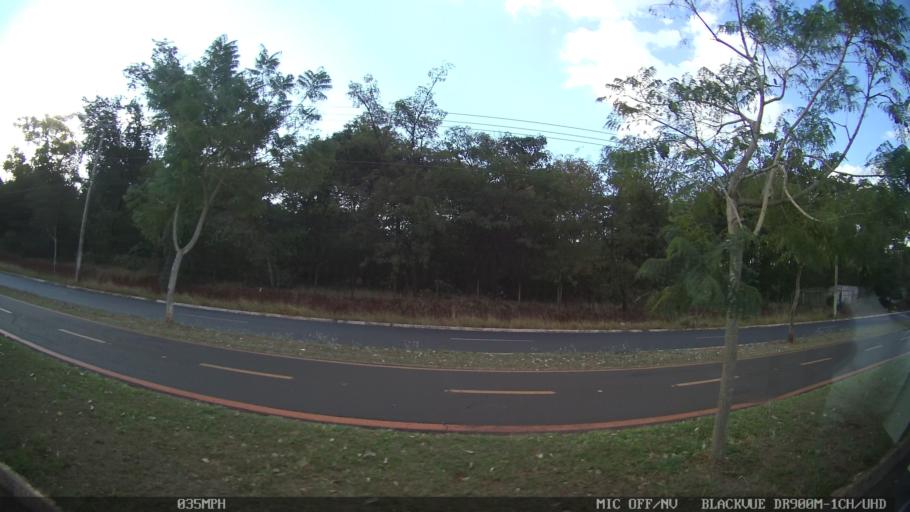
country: BR
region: Sao Paulo
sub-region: Ribeirao Preto
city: Ribeirao Preto
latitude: -21.1936
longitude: -47.7463
